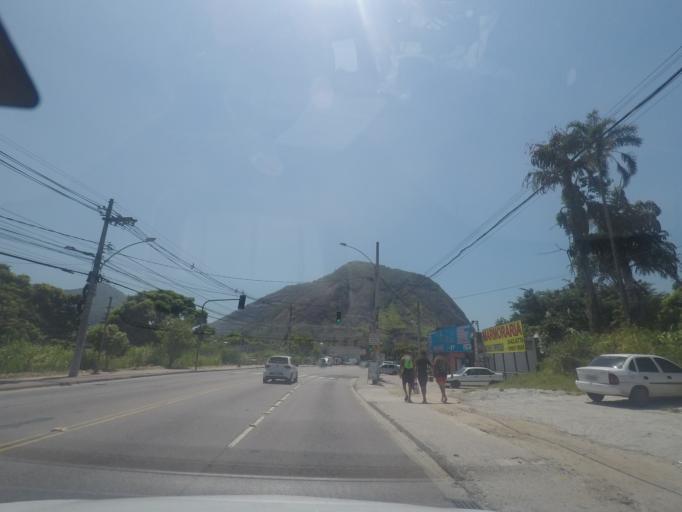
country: BR
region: Rio de Janeiro
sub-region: Nilopolis
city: Nilopolis
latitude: -22.9859
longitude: -43.4584
